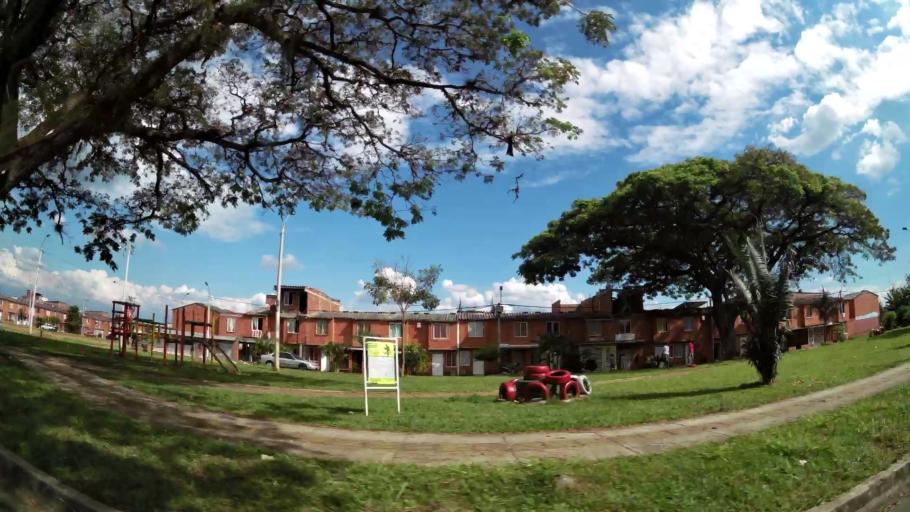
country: CO
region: Valle del Cauca
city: Cali
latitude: 3.3929
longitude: -76.5110
